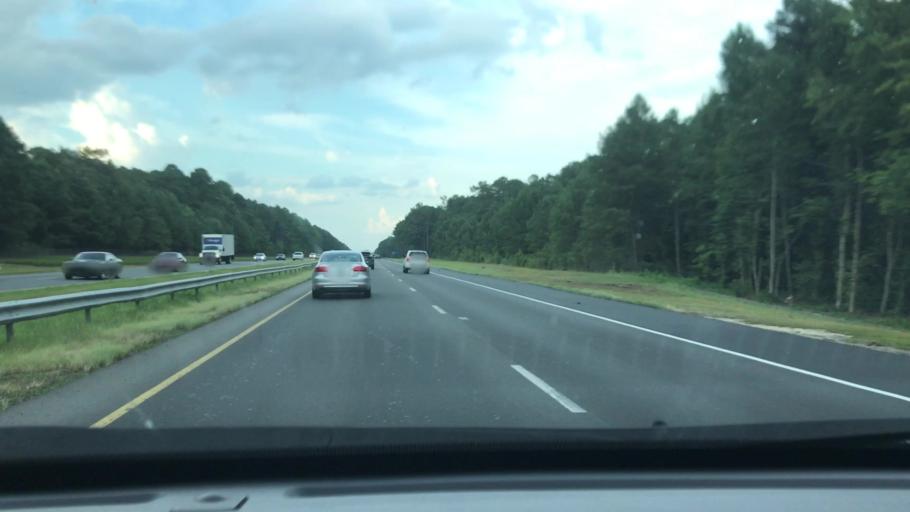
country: US
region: North Carolina
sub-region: Cumberland County
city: Eastover
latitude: 35.1441
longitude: -78.7320
